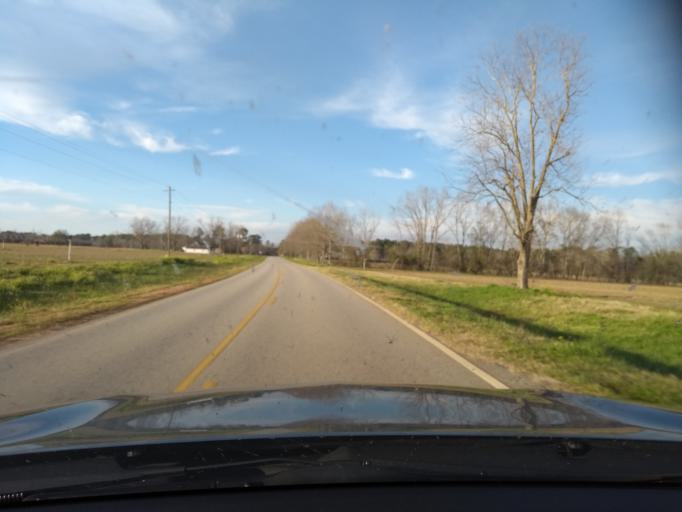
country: US
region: Georgia
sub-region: Bulloch County
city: Statesboro
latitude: 32.3353
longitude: -81.7736
